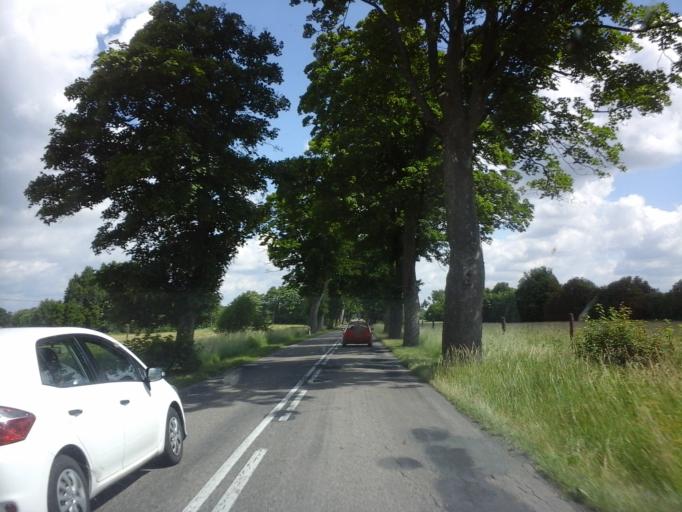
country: PL
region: West Pomeranian Voivodeship
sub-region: Powiat swidwinski
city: Swidwin
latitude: 53.7466
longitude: 15.7268
